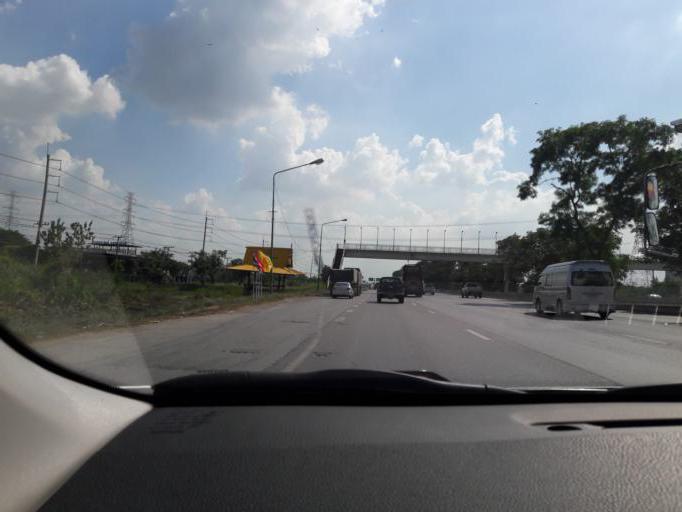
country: TH
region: Phra Nakhon Si Ayutthaya
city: Bang Pa-in
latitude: 14.2405
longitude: 100.6123
